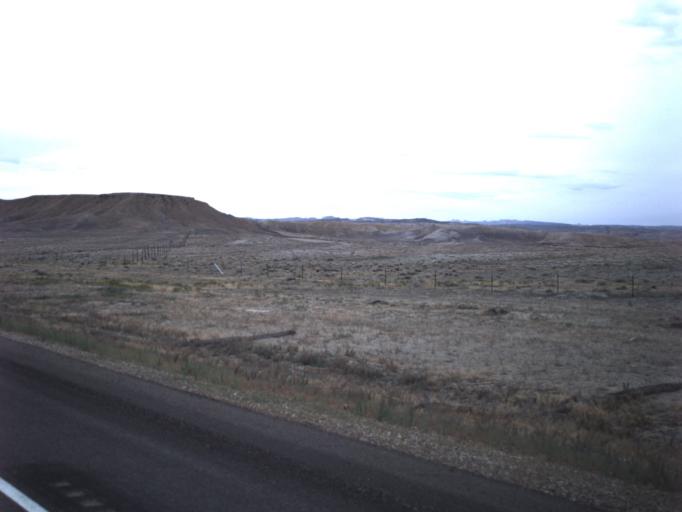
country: US
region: Utah
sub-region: Carbon County
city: East Carbon City
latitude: 39.3017
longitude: -110.3575
